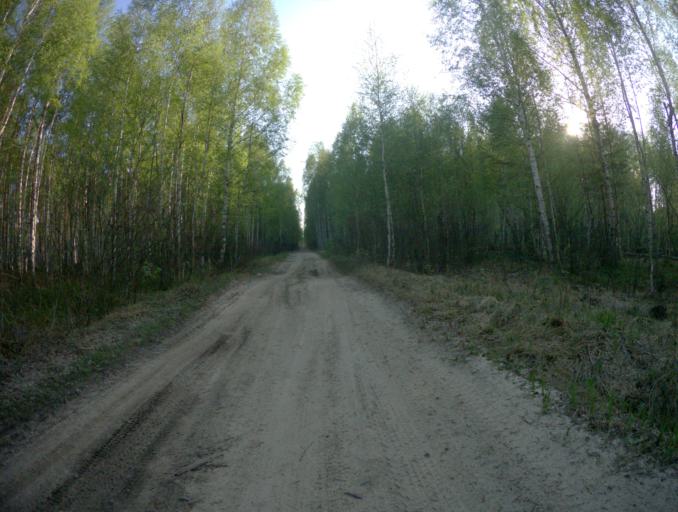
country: RU
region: Vladimir
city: Vyazniki
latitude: 56.3750
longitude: 42.1709
